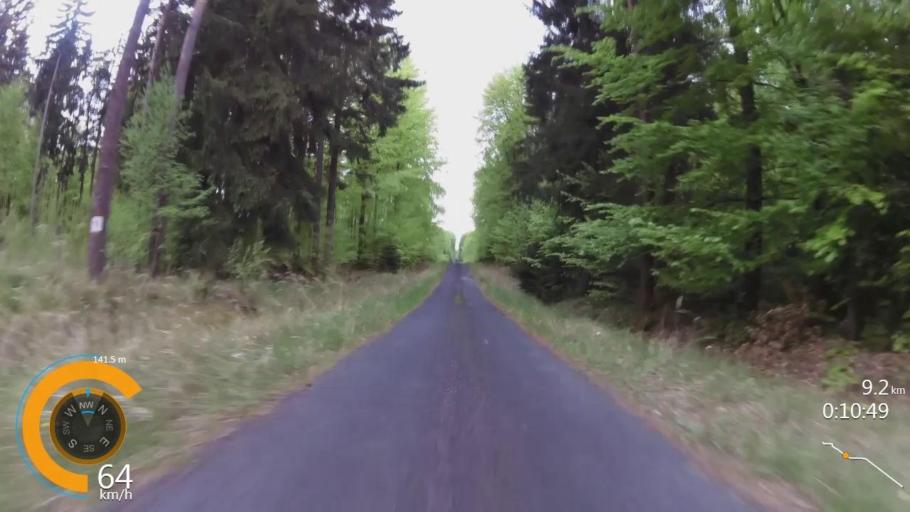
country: PL
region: West Pomeranian Voivodeship
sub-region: Powiat drawski
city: Wierzchowo
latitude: 53.5083
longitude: 16.1205
